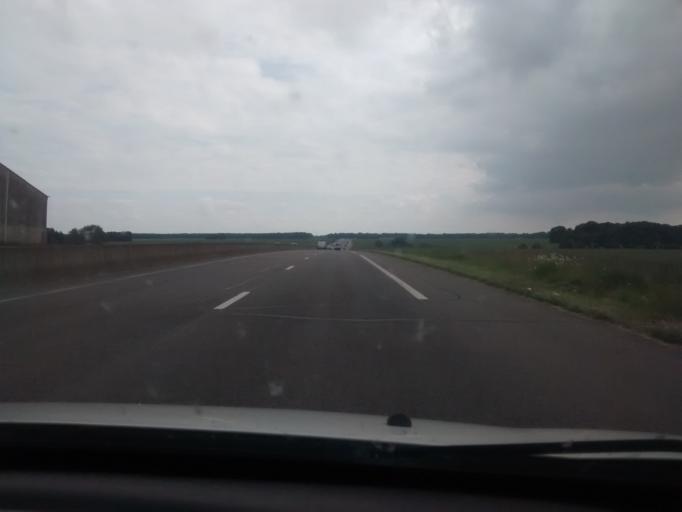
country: FR
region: Ile-de-France
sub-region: Departement des Yvelines
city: Ablis
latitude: 48.5628
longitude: 1.8321
